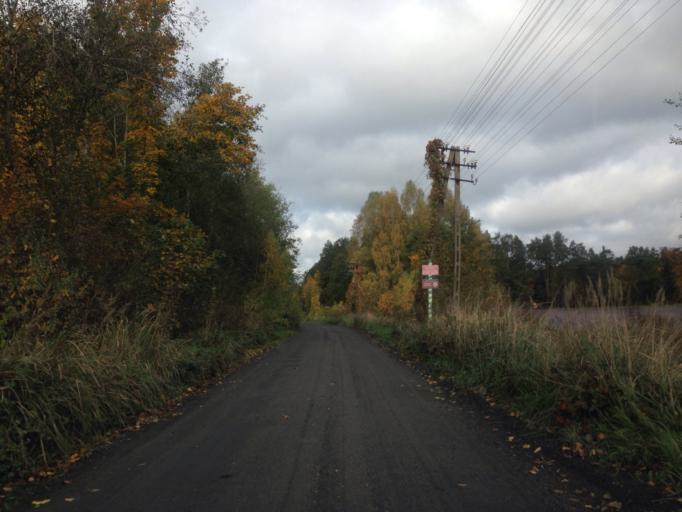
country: PL
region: Kujawsko-Pomorskie
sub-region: Powiat brodnicki
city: Bartniczka
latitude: 53.2642
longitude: 19.5838
